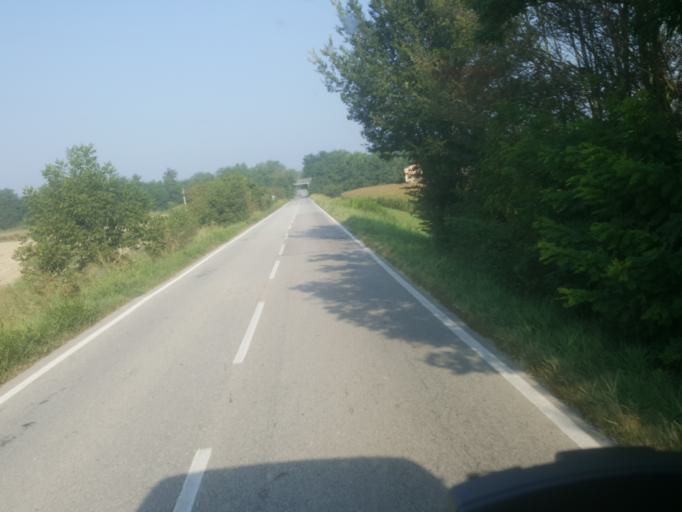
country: IT
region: Emilia-Romagna
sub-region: Provincia di Ravenna
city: Lavezzola
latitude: 44.5727
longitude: 11.8830
